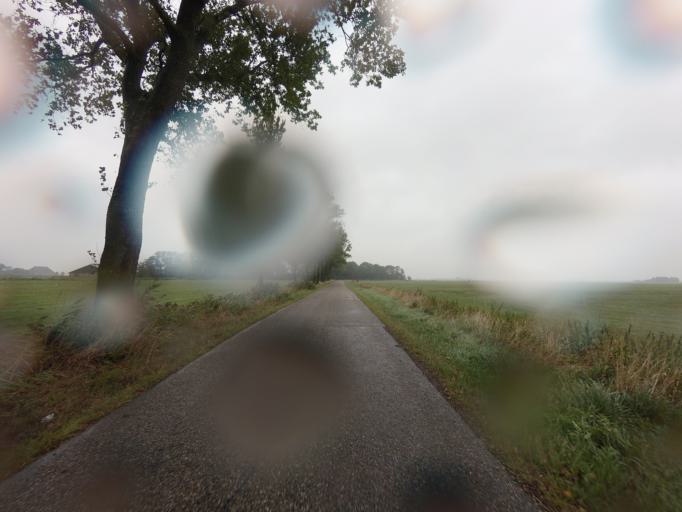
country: NL
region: Friesland
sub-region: Gemeente Boarnsterhim
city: Aldeboarn
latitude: 53.0723
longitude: 5.9287
